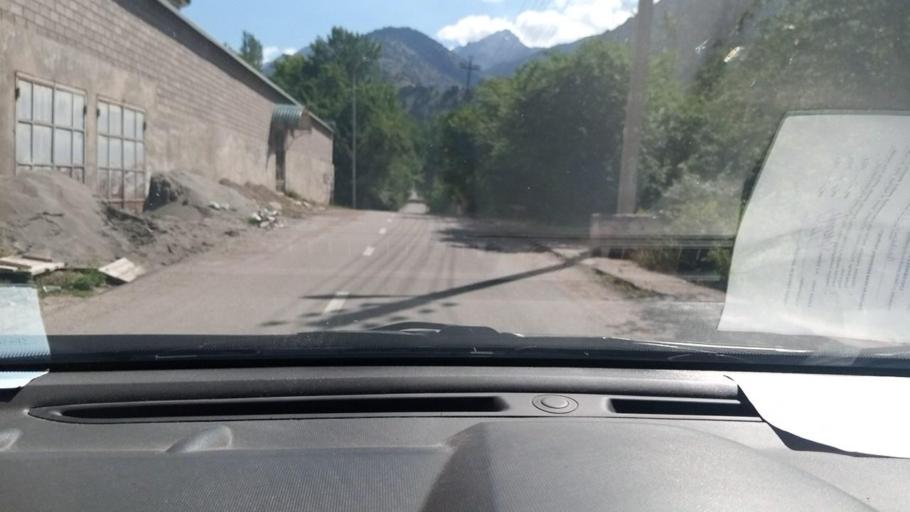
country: UZ
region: Toshkent
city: Yangiobod
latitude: 41.1217
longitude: 70.1004
